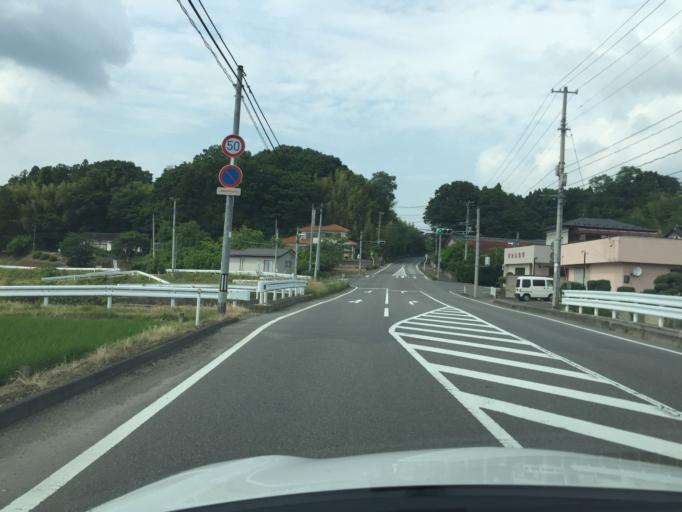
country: JP
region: Fukushima
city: Sukagawa
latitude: 37.2733
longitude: 140.4197
